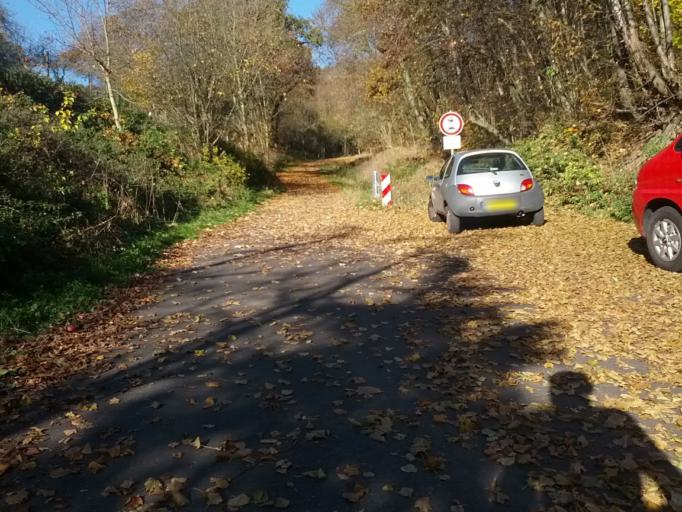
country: DE
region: Thuringia
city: Seebach
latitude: 50.9456
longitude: 10.4602
